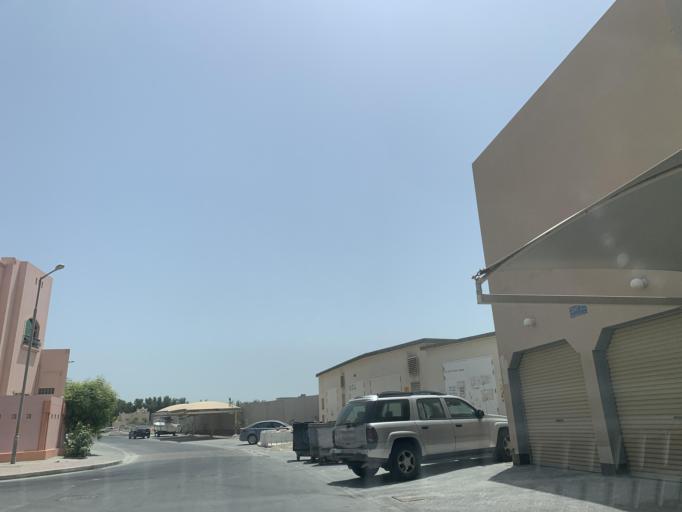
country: BH
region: Northern
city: Madinat `Isa
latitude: 26.1615
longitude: 50.5776
